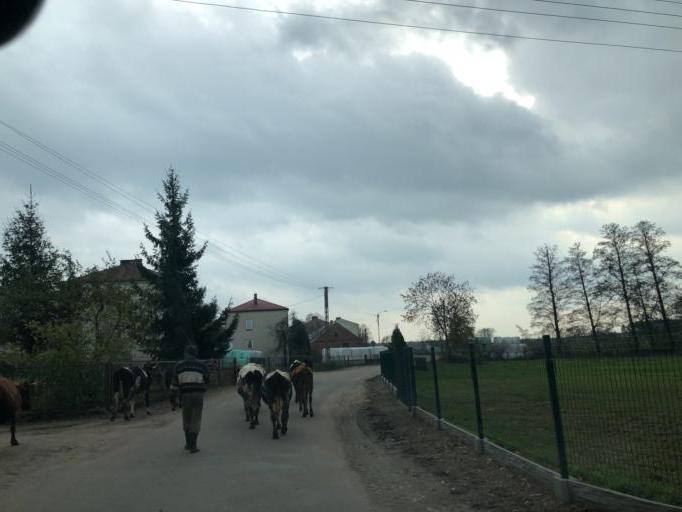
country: PL
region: Podlasie
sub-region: Lomza
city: Lomza
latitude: 53.1565
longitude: 22.0033
